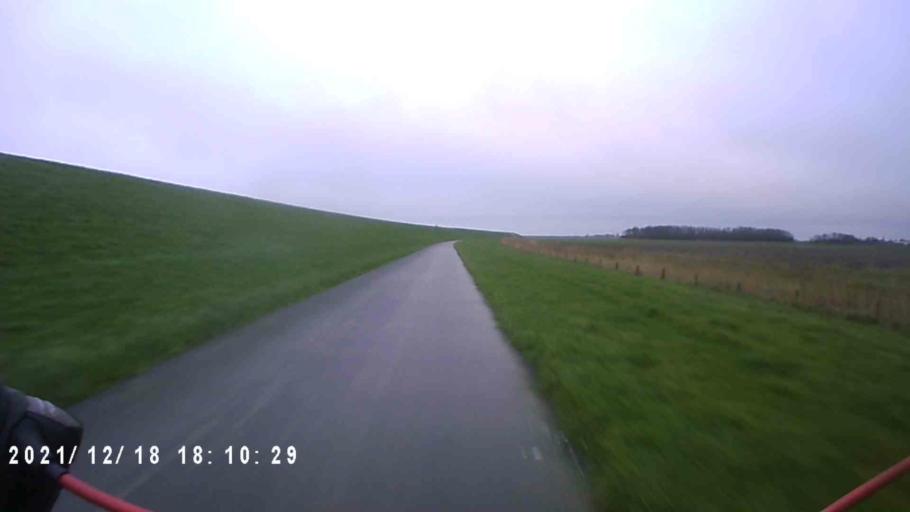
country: NL
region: Friesland
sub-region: Gemeente Dongeradeel
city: Ternaard
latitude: 53.3883
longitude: 5.9376
